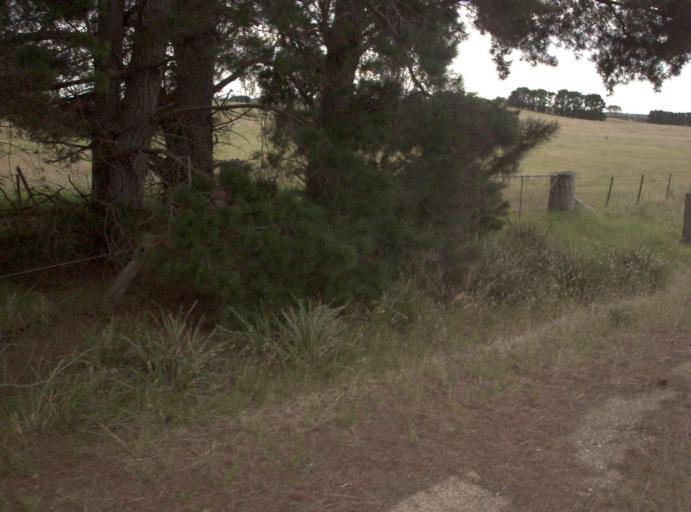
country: AU
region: Victoria
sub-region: East Gippsland
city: Bairnsdale
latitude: -37.9993
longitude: 147.3707
